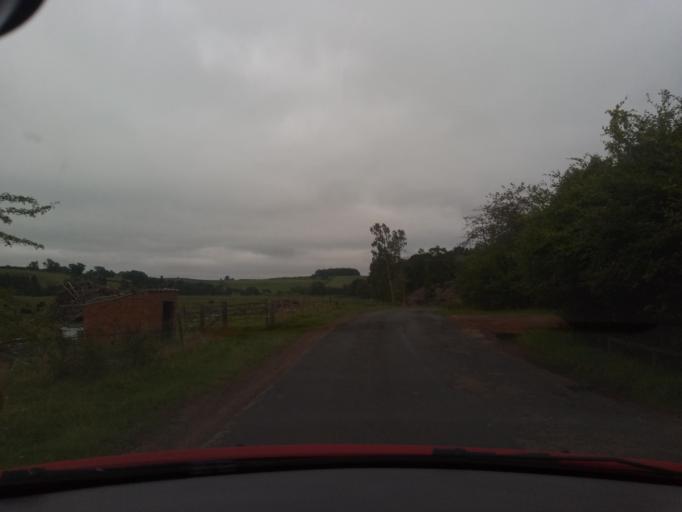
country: GB
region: England
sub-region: Northumberland
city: Otterburn
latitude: 55.3300
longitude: -2.0858
